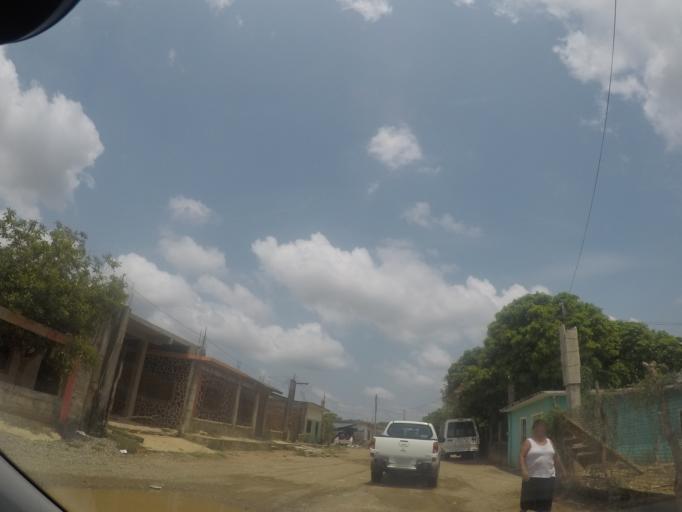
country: MX
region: Oaxaca
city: El Espinal
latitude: 16.5514
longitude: -94.9429
